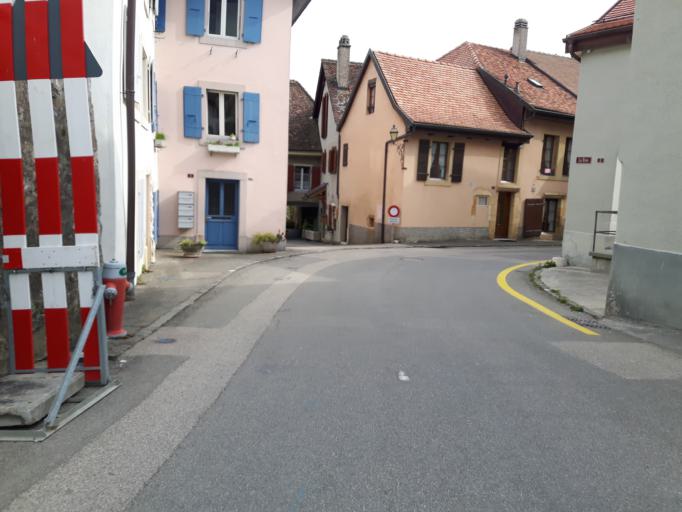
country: CH
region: Vaud
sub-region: Jura-Nord vaudois District
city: Yvonand
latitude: 46.8498
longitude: 6.7198
